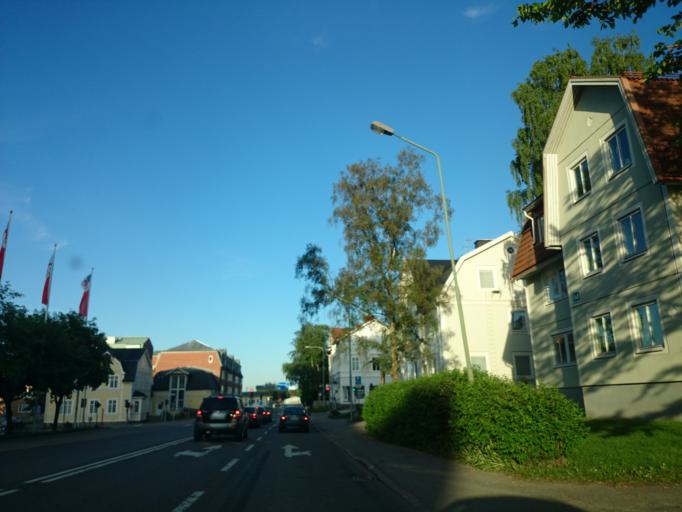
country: SE
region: Vaesternorrland
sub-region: Sundsvalls Kommun
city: Sundsvall
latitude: 62.3858
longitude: 17.3077
